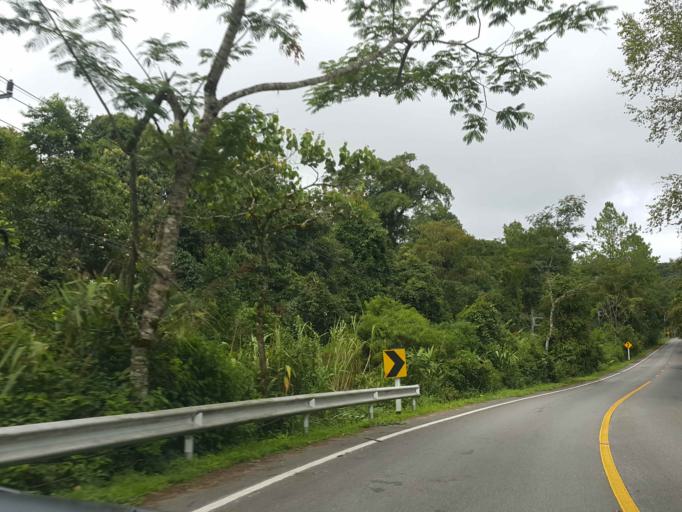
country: TH
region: Chiang Mai
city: Mae Chaem
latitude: 18.5300
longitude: 98.4960
